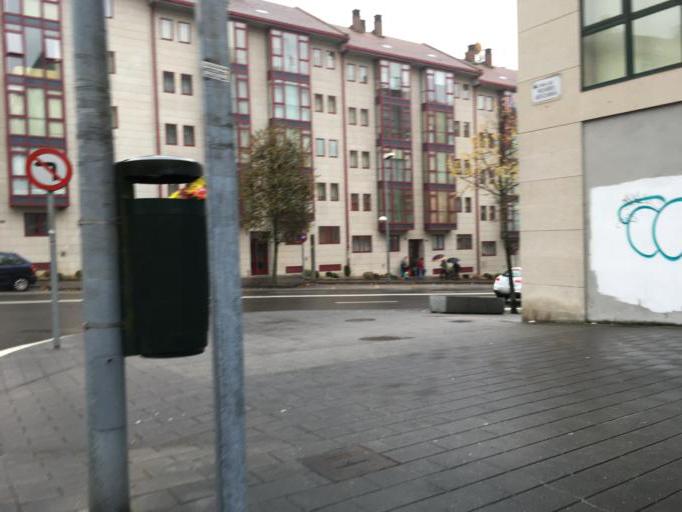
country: ES
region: Galicia
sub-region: Provincia da Coruna
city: Santiago de Compostela
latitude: 42.8682
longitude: -8.5549
